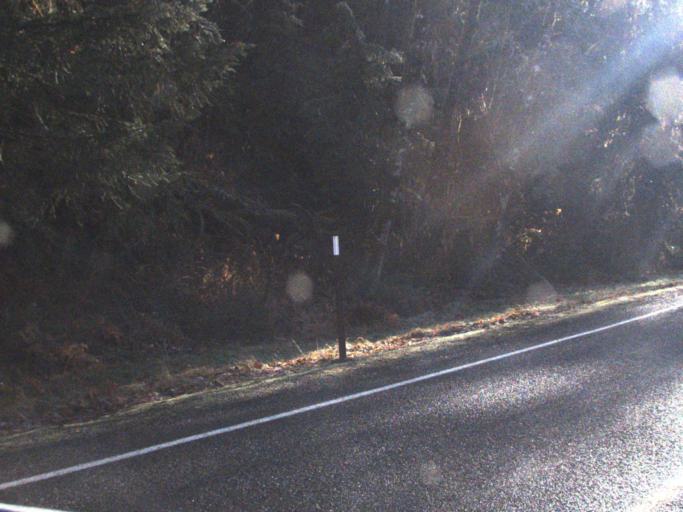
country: US
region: Washington
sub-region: Snohomish County
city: Darrington
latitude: 48.3902
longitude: -121.5500
